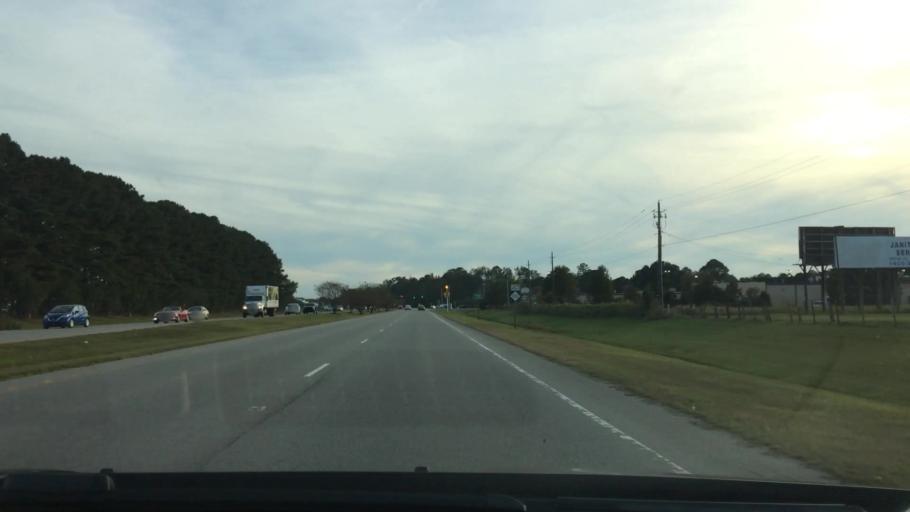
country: US
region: North Carolina
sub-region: Pitt County
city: Ayden
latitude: 35.4788
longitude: -77.4339
